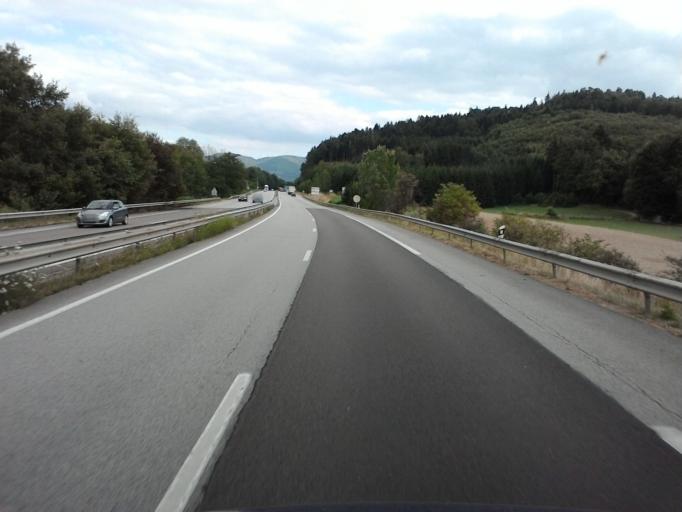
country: FR
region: Lorraine
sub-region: Departement des Vosges
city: Eloyes
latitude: 48.0950
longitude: 6.5911
